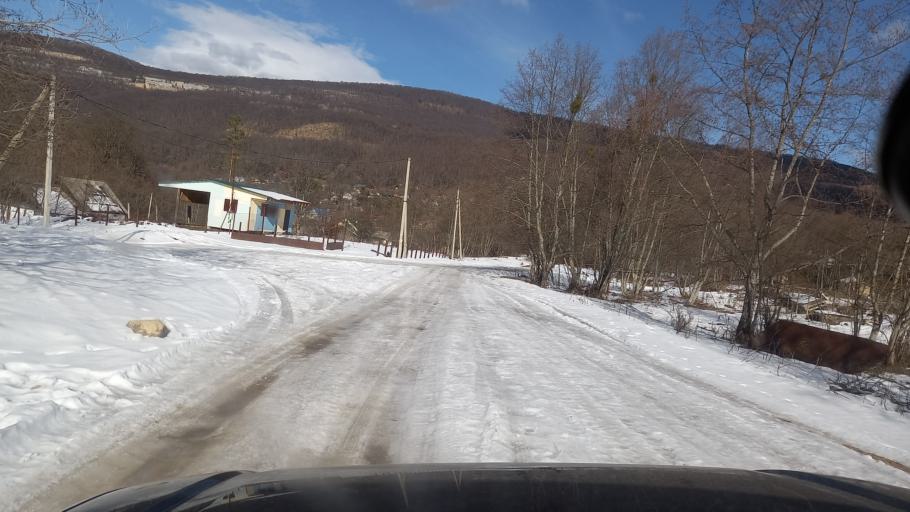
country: RU
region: Adygeya
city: Kamennomostskiy
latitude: 44.1938
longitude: 39.9607
